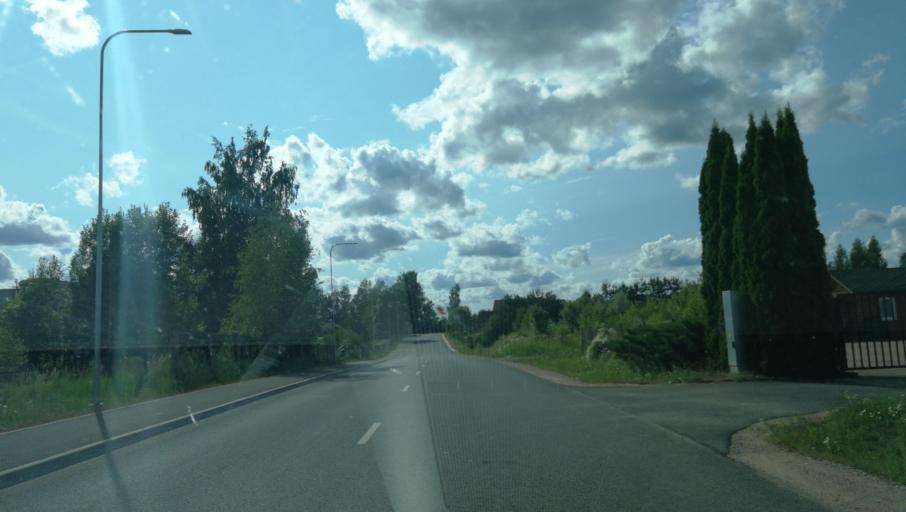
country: LV
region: Cesu Rajons
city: Cesis
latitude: 57.3232
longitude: 25.3028
